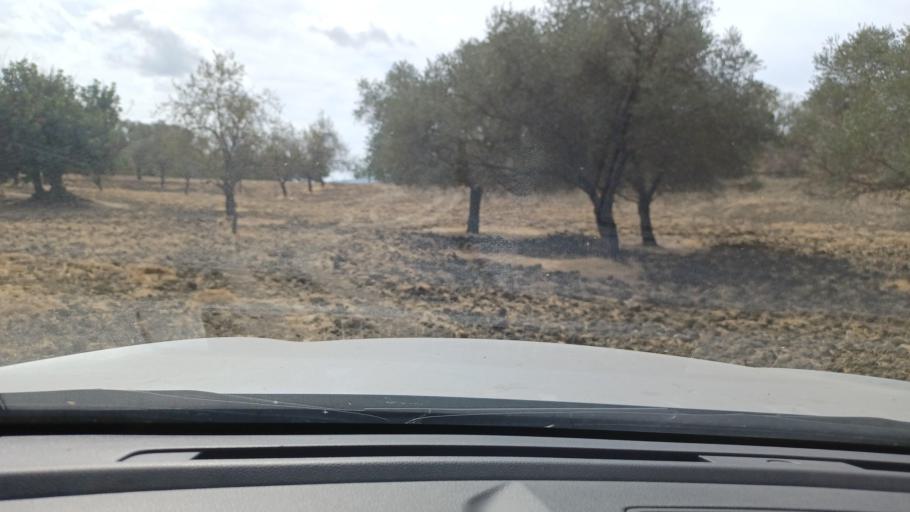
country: CY
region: Pafos
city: Polis
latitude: 35.0062
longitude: 32.5401
